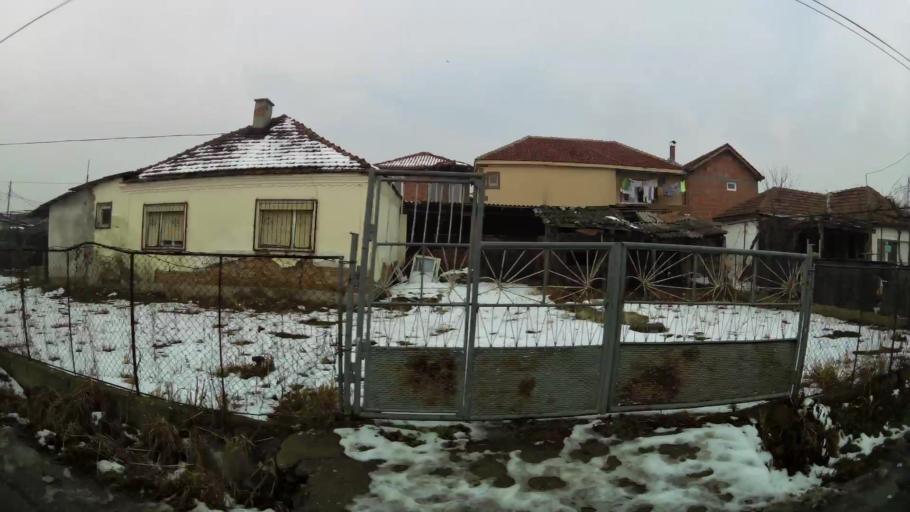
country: MK
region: Ilinden
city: Jurumleri
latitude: 41.9671
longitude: 21.5612
